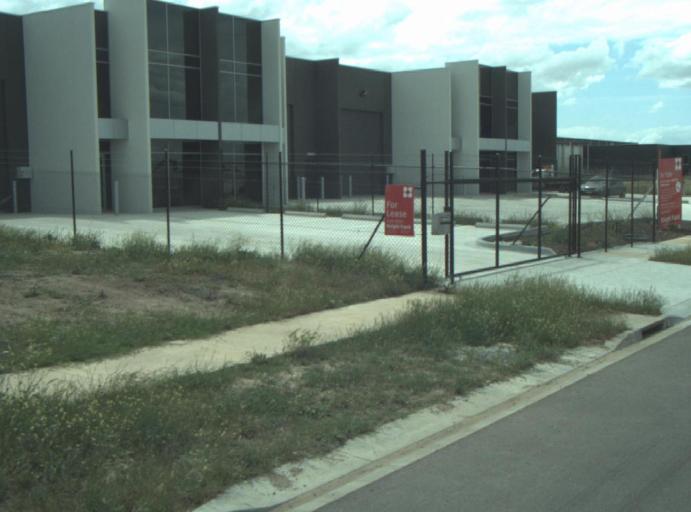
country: AU
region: Victoria
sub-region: Greater Geelong
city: Bell Park
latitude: -38.0980
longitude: 144.3427
